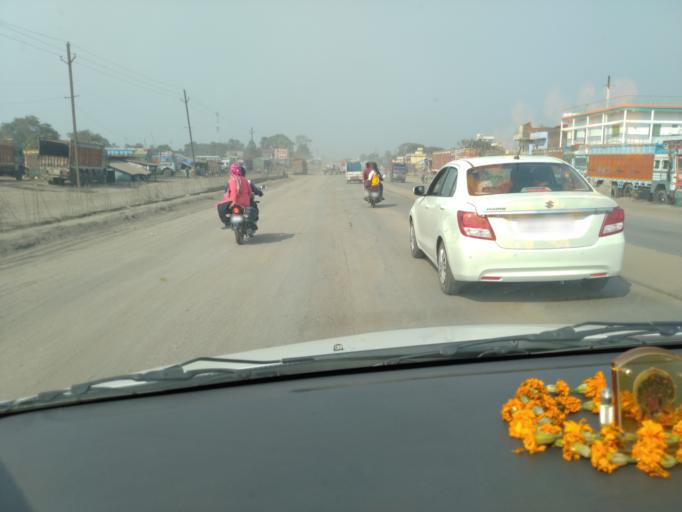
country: IN
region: Bihar
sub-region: Rohtas
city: Dehri
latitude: 24.9139
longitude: 84.1616
